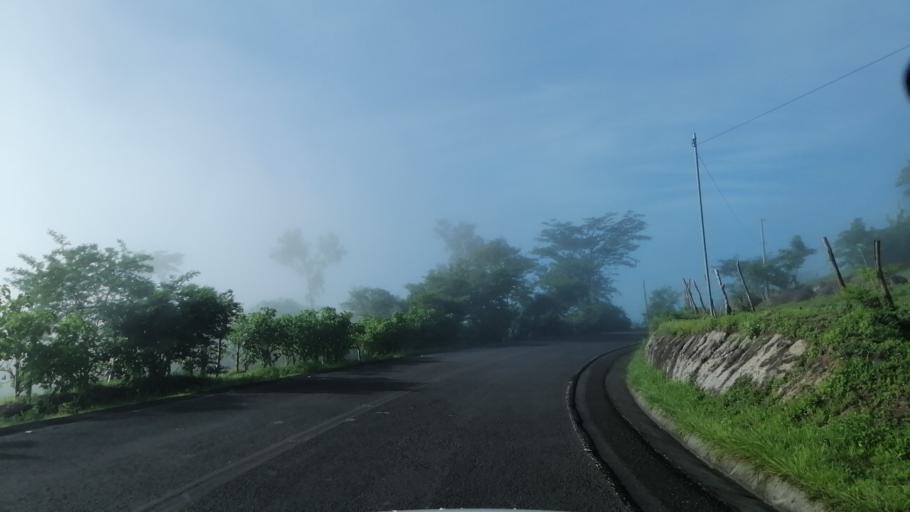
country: SV
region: Morazan
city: Cacaopera
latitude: 13.7900
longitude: -88.1185
